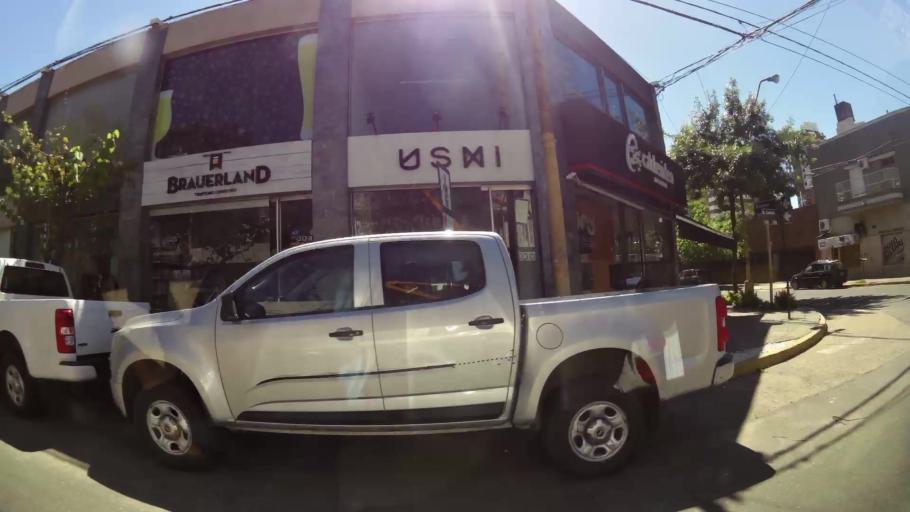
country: AR
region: Santa Fe
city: Santa Fe de la Vera Cruz
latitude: -31.6384
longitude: -60.6959
